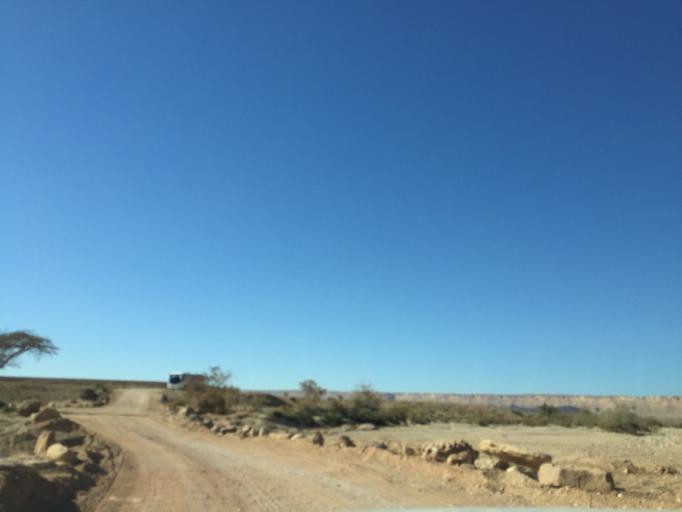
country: IL
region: Southern District
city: Mitzpe Ramon
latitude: 30.6237
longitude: 34.9272
